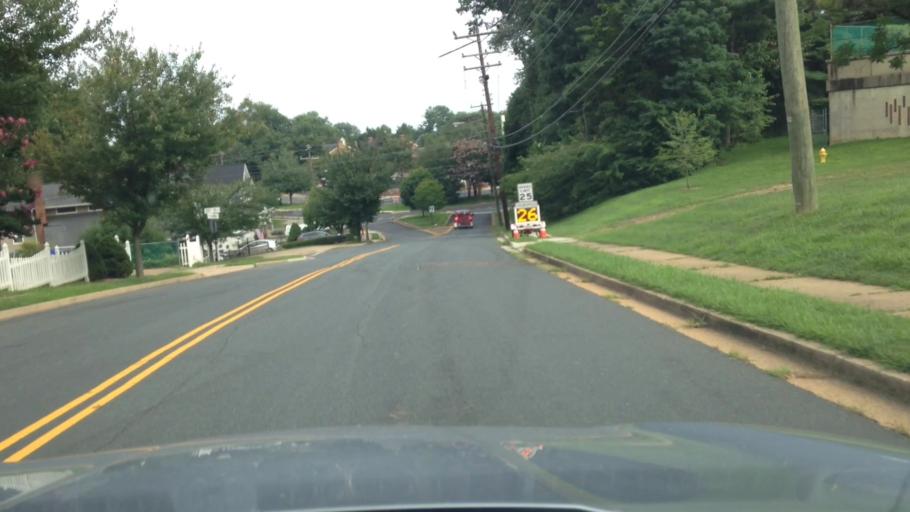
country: US
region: Virginia
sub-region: City of Falls Church
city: Falls Church
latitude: 38.9017
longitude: -77.1577
